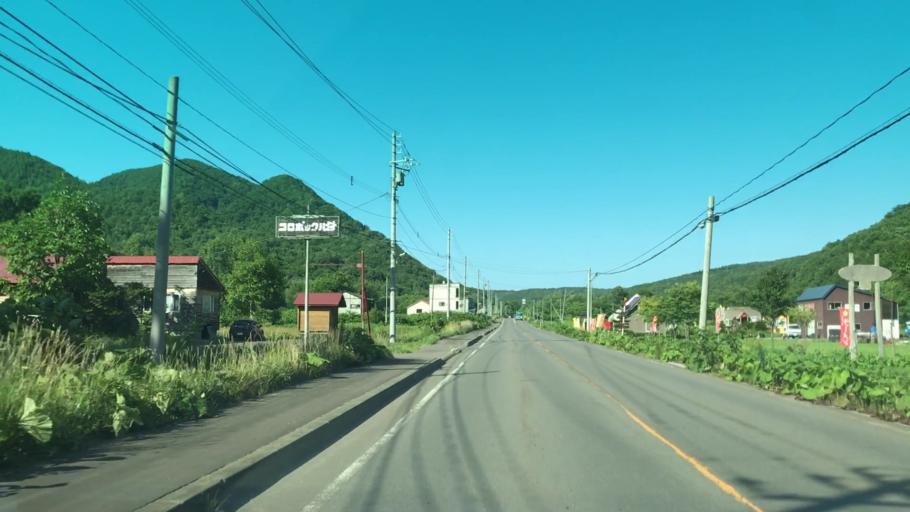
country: JP
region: Hokkaido
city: Yoichi
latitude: 43.0533
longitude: 140.8601
